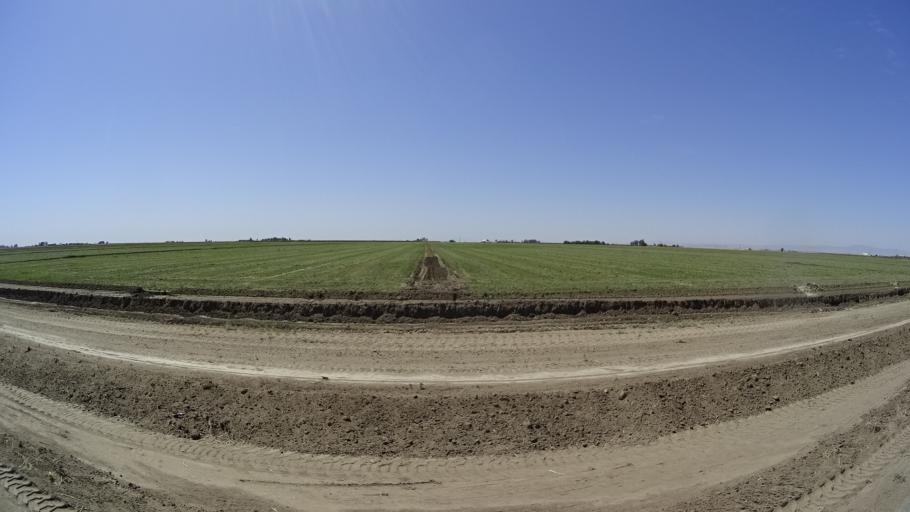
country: US
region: California
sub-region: Kings County
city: Stratford
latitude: 36.1894
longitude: -119.8068
